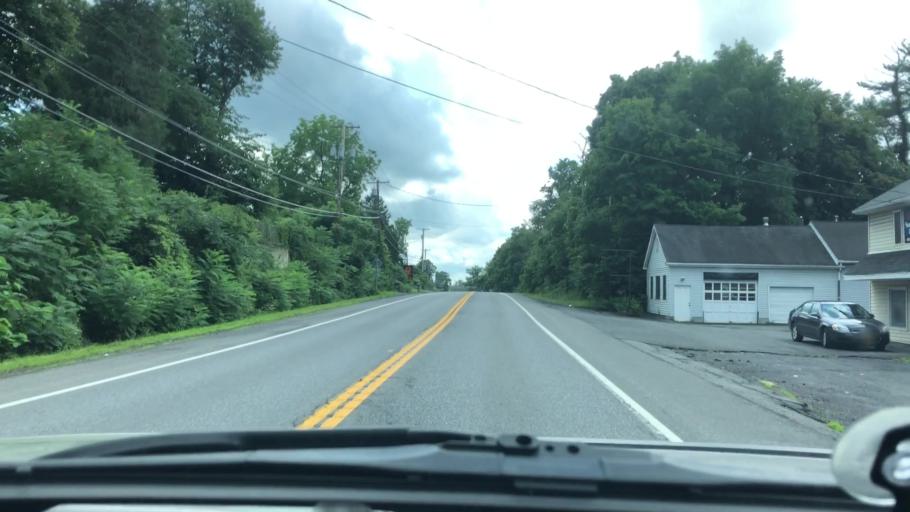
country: US
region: New York
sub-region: Ulster County
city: Saugerties
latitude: 42.0947
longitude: -73.9723
